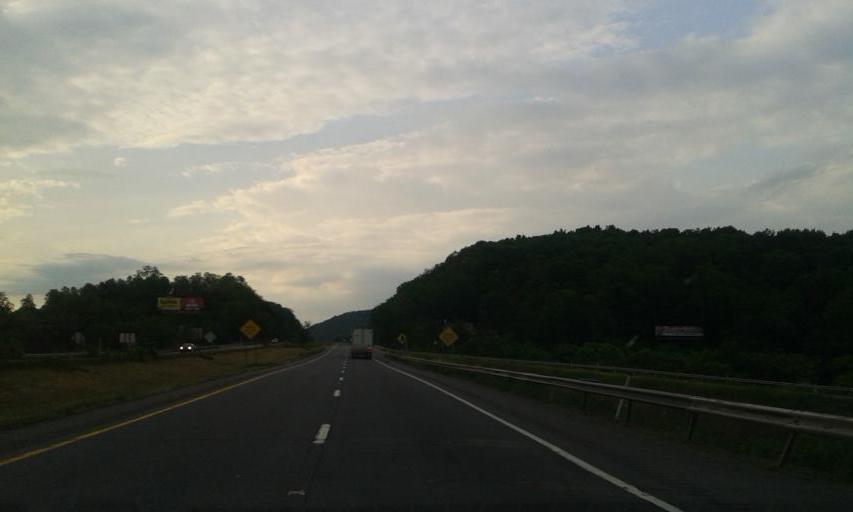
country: US
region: Pennsylvania
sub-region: Susquehanna County
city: Hallstead
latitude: 41.9672
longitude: -75.7385
